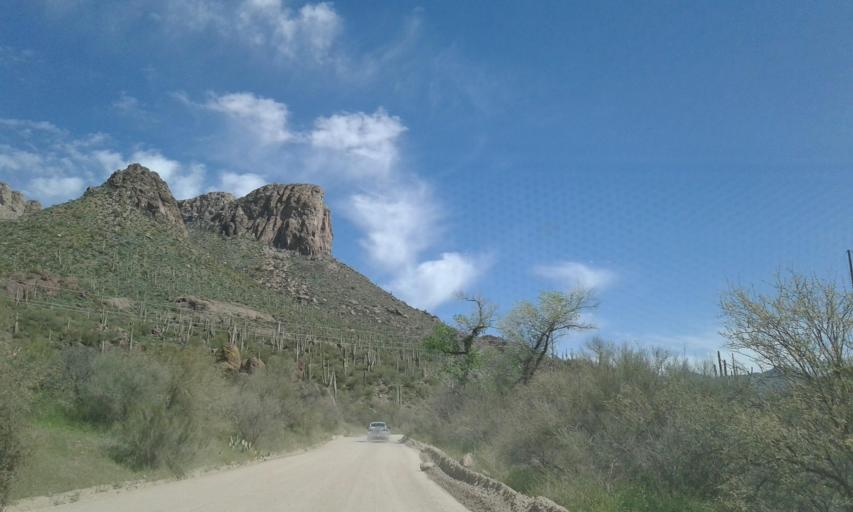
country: US
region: Arizona
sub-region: Pinal County
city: Gold Camp
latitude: 33.5381
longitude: -111.2752
